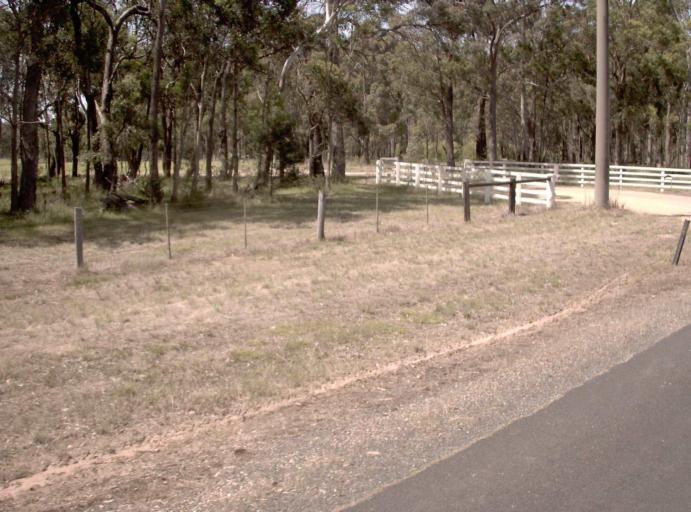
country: AU
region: Victoria
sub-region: Wellington
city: Sale
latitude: -37.9224
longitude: 147.2445
